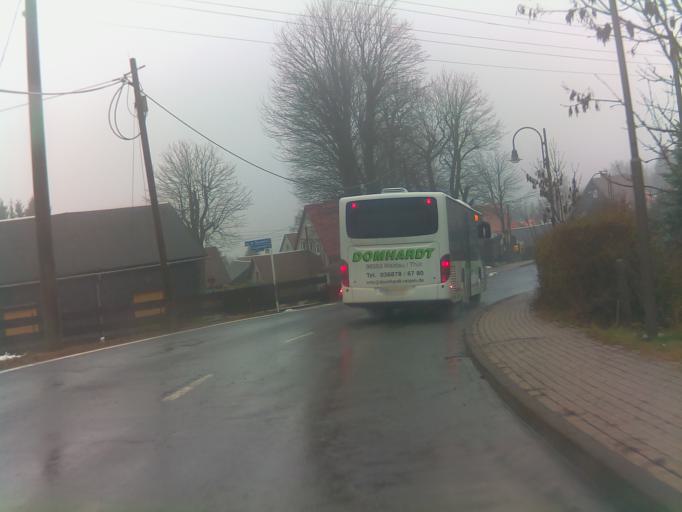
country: DE
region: Thuringia
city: Eisfeld
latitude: 50.4986
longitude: 10.9031
